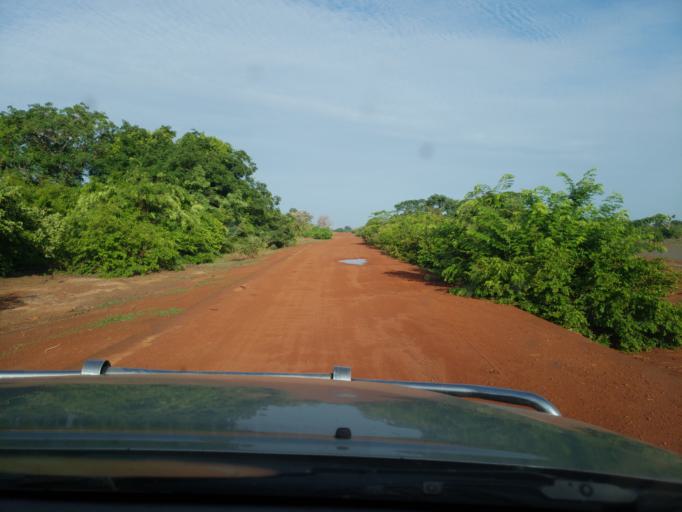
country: ML
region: Sikasso
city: Koutiala
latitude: 12.4240
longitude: -5.6664
